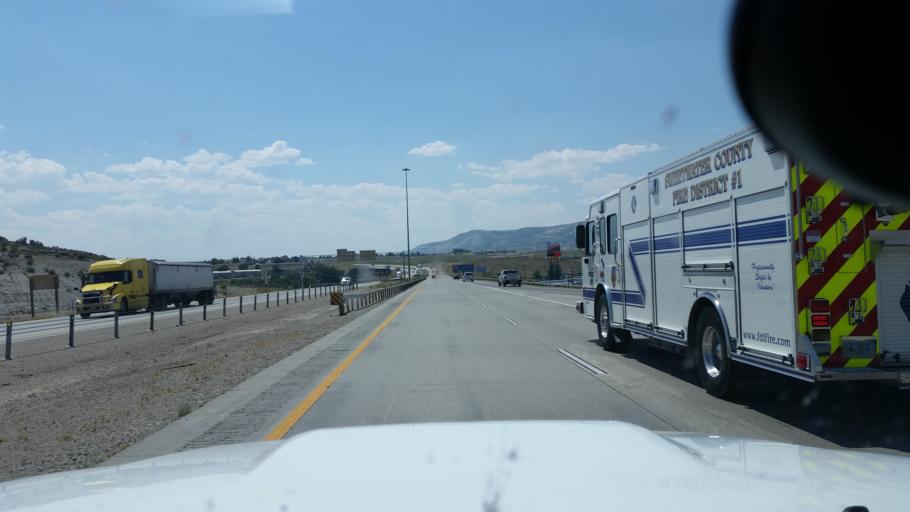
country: US
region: Wyoming
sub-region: Sweetwater County
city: Rock Springs
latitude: 41.6090
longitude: -109.2264
